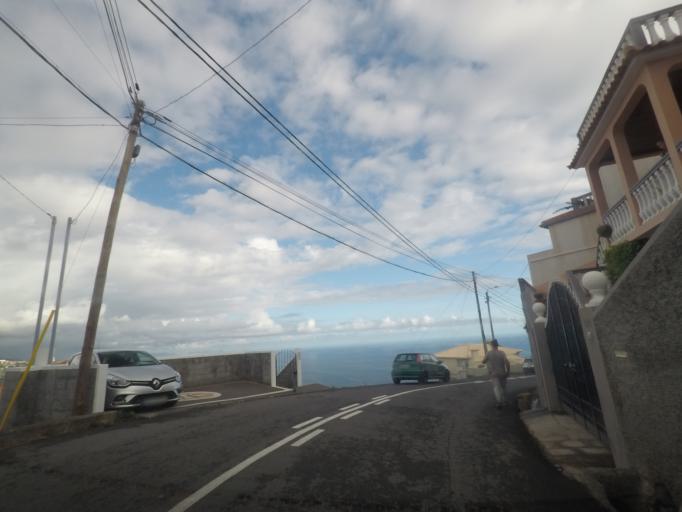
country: PT
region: Madeira
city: Camara de Lobos
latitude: 32.6553
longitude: -16.9917
